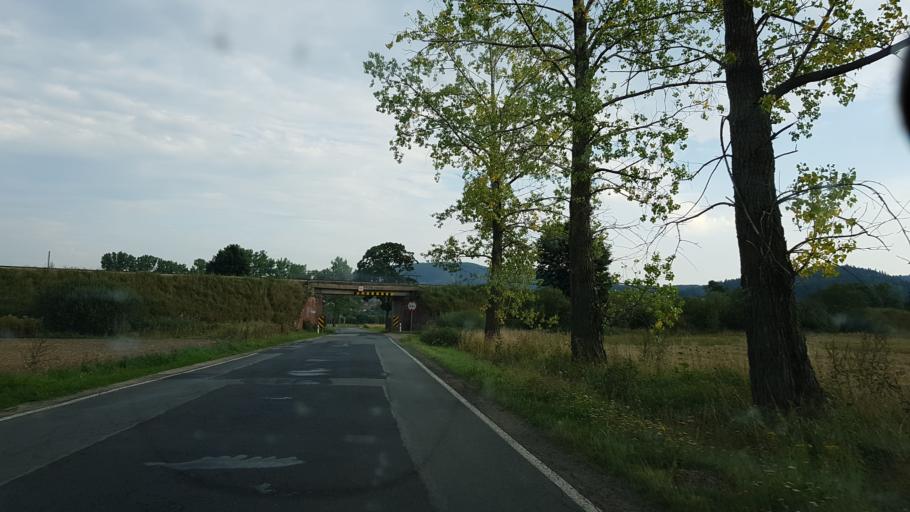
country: PL
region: Lower Silesian Voivodeship
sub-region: Powiat kamiennogorski
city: Marciszow
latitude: 50.8609
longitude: 16.0019
